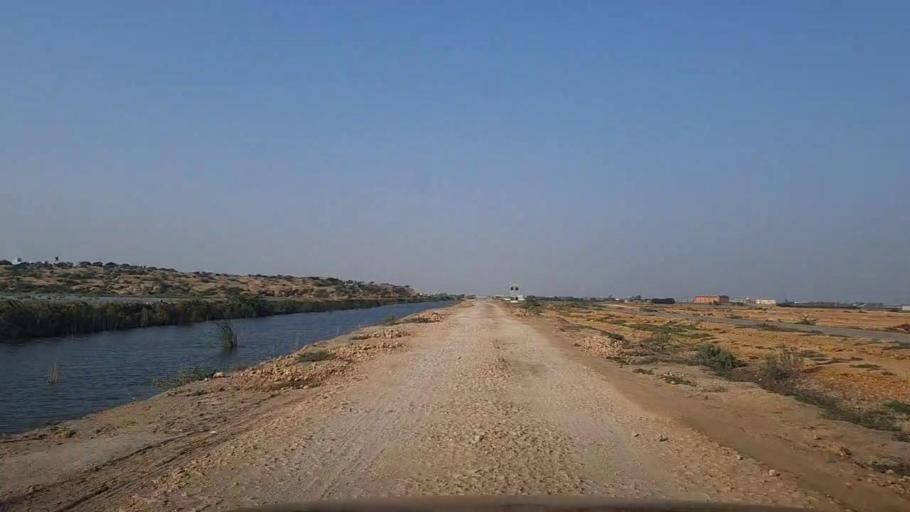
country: PK
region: Sindh
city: Thatta
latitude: 24.7393
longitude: 67.9065
